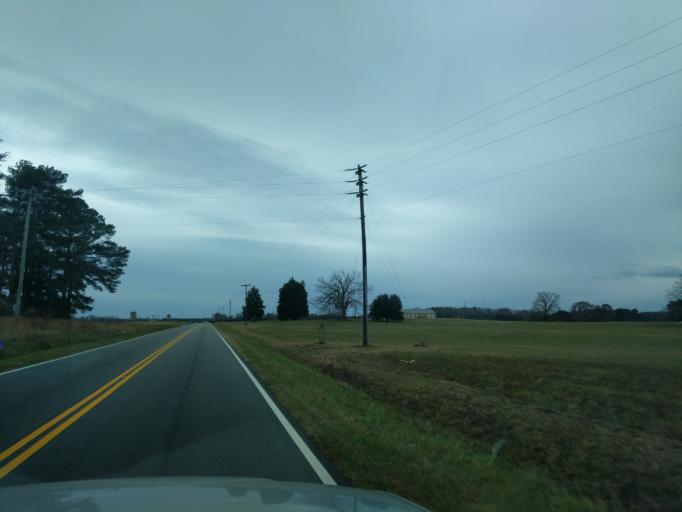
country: US
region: South Carolina
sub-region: Laurens County
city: Laurens
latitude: 34.3711
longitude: -81.9941
